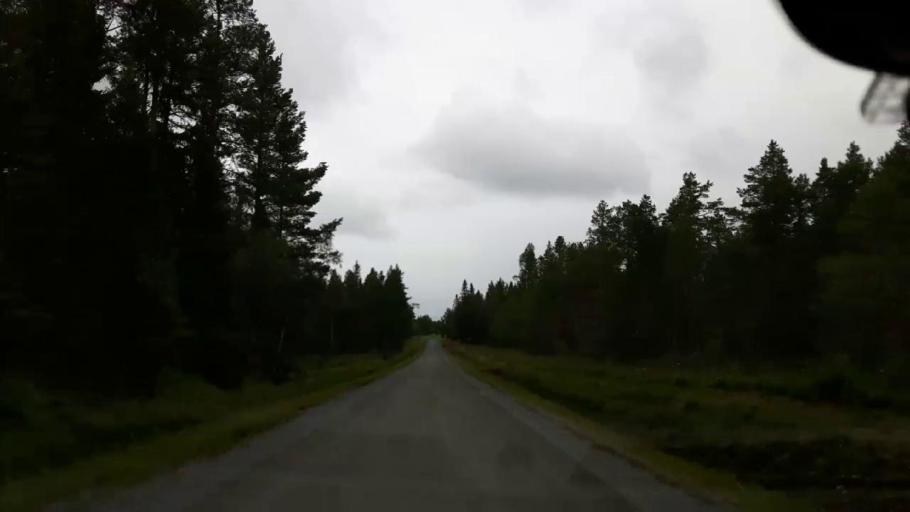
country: SE
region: Jaemtland
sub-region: OEstersunds Kommun
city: Ostersund
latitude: 63.0827
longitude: 14.5549
